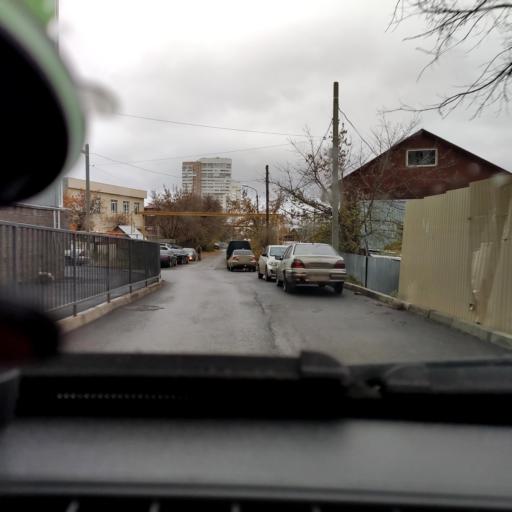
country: RU
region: Bashkortostan
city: Ufa
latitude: 54.7106
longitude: 55.9861
